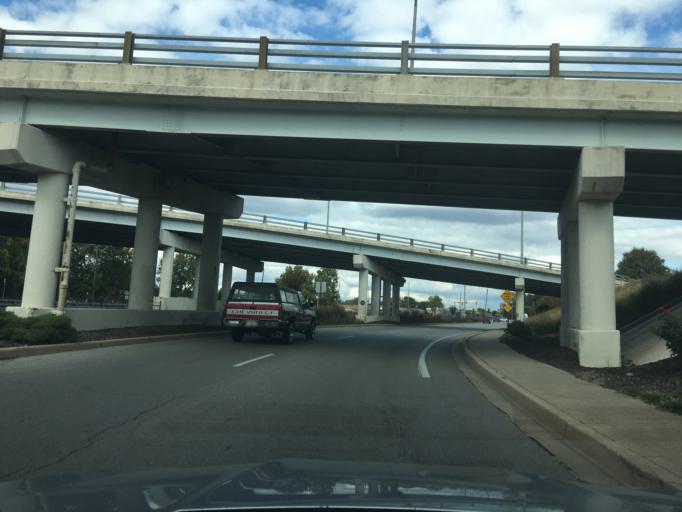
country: US
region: Indiana
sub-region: Tippecanoe County
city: West Lafayette
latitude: 40.4249
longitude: -86.8930
